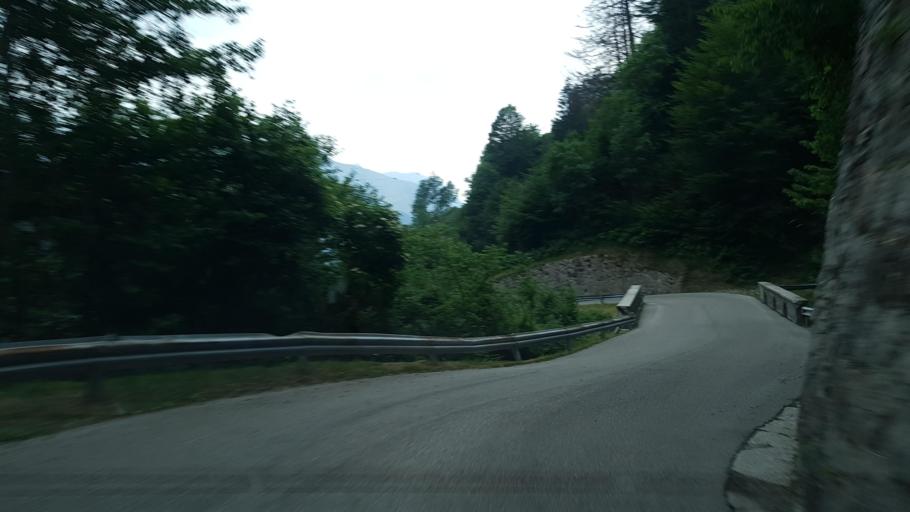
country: IT
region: Friuli Venezia Giulia
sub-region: Provincia di Udine
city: Pontebba
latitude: 46.5253
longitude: 13.2992
